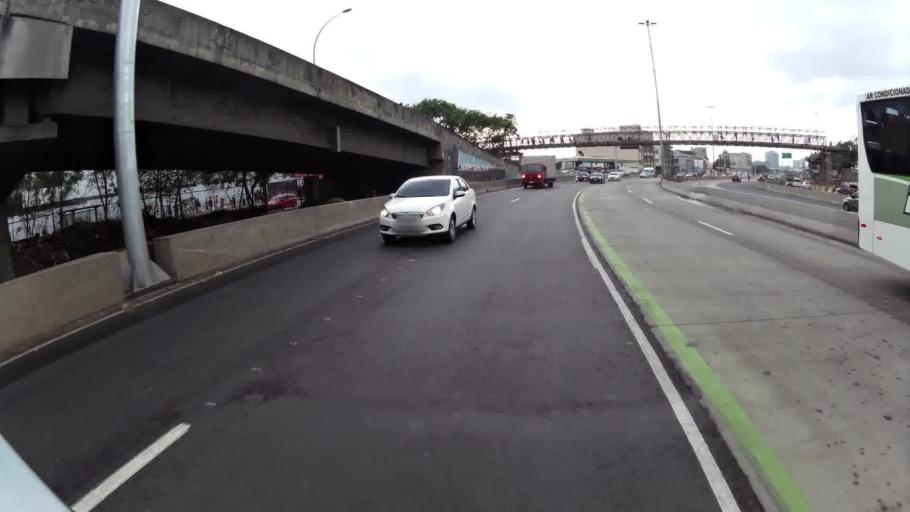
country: BR
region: Rio de Janeiro
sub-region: Rio De Janeiro
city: Rio de Janeiro
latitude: -22.8848
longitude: -43.2270
